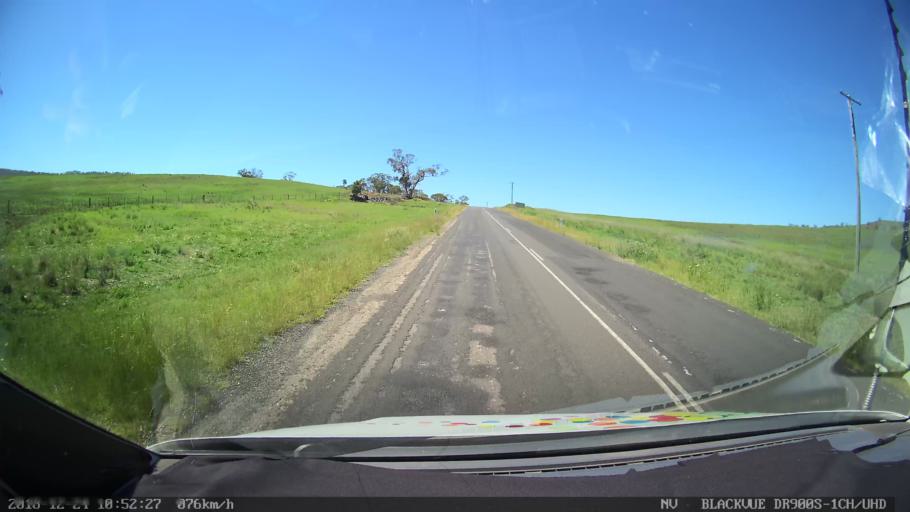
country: AU
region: New South Wales
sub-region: Upper Hunter Shire
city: Merriwa
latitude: -31.9806
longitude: 150.4221
